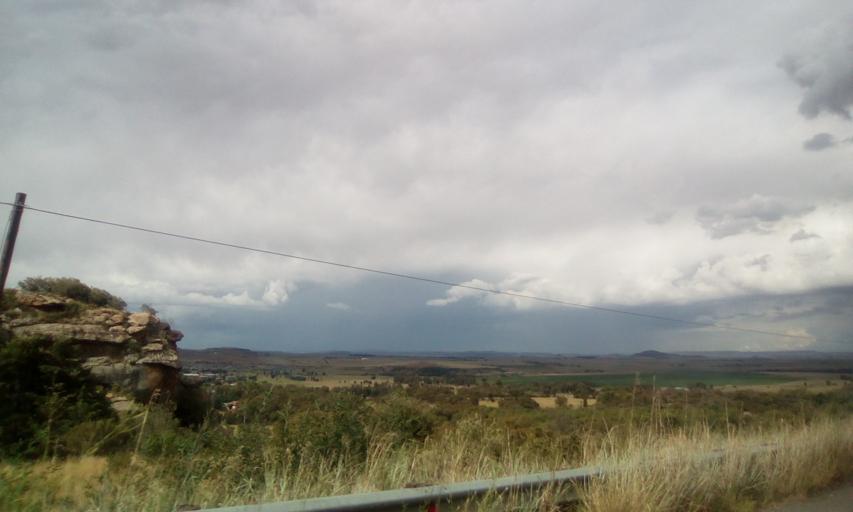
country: ZA
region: Orange Free State
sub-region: Thabo Mofutsanyana District Municipality
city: Ladybrand
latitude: -29.2125
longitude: 27.4569
